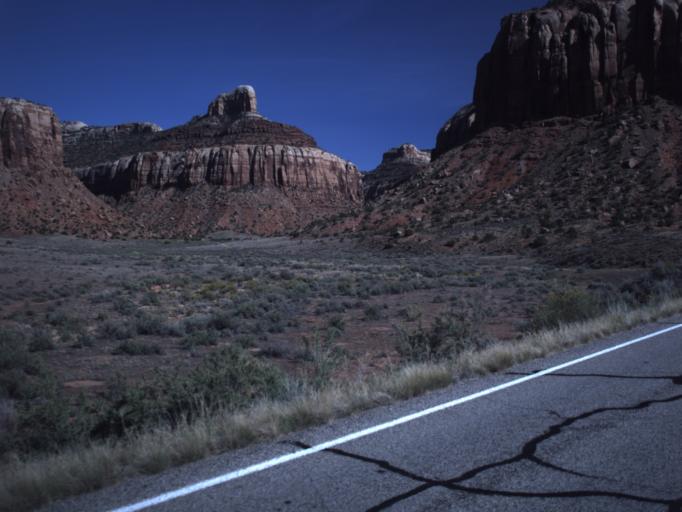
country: US
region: Utah
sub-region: San Juan County
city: Monticello
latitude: 38.0670
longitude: -109.5542
